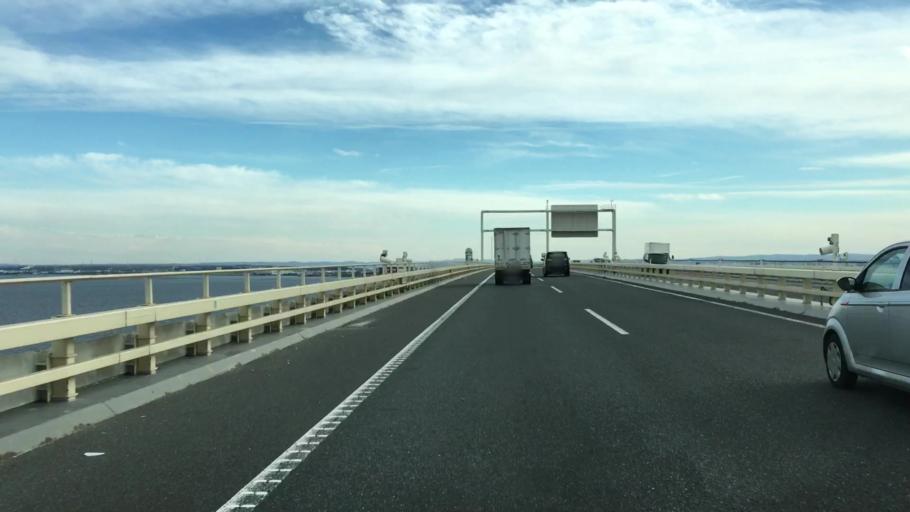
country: JP
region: Chiba
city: Kisarazu
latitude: 35.4565
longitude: 139.8861
